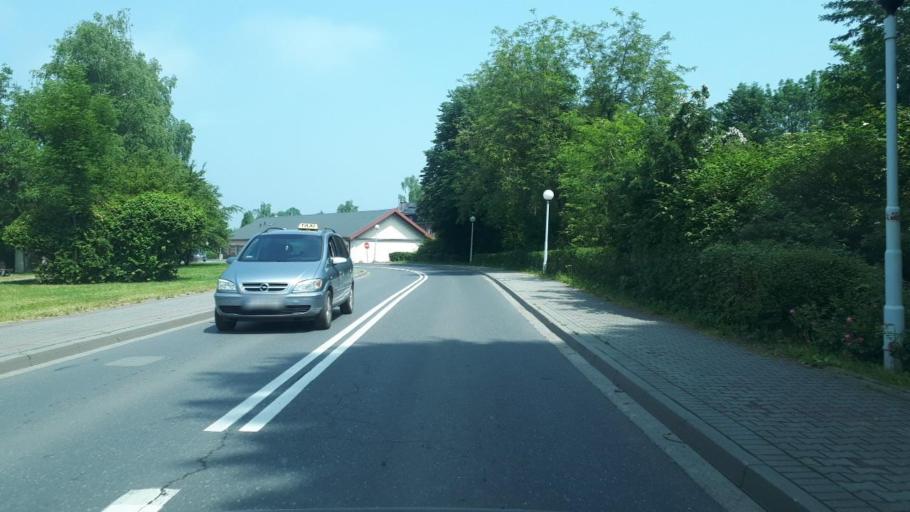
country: PL
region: Silesian Voivodeship
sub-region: Powiat cieszynski
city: Ustron
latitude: 49.7243
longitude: 18.8079
